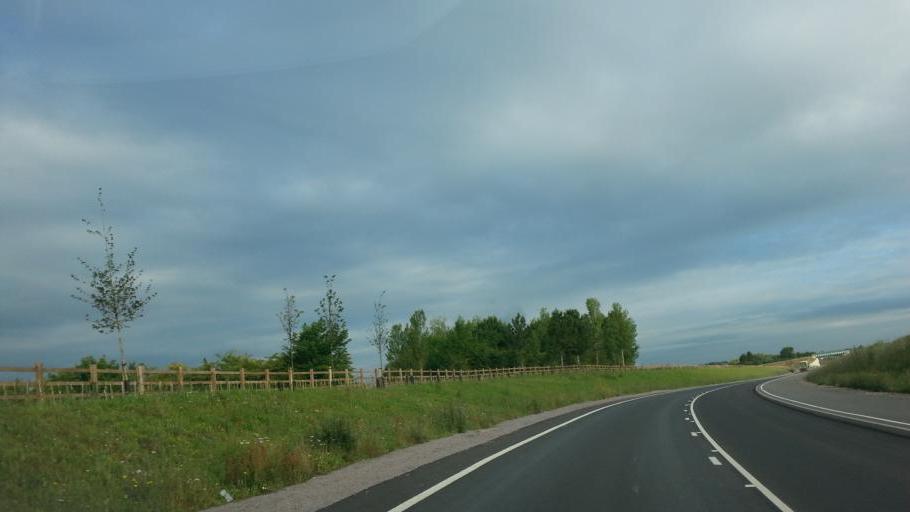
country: GB
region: England
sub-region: Nottinghamshire
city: Newark on Trent
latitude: 53.0468
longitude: -0.7956
